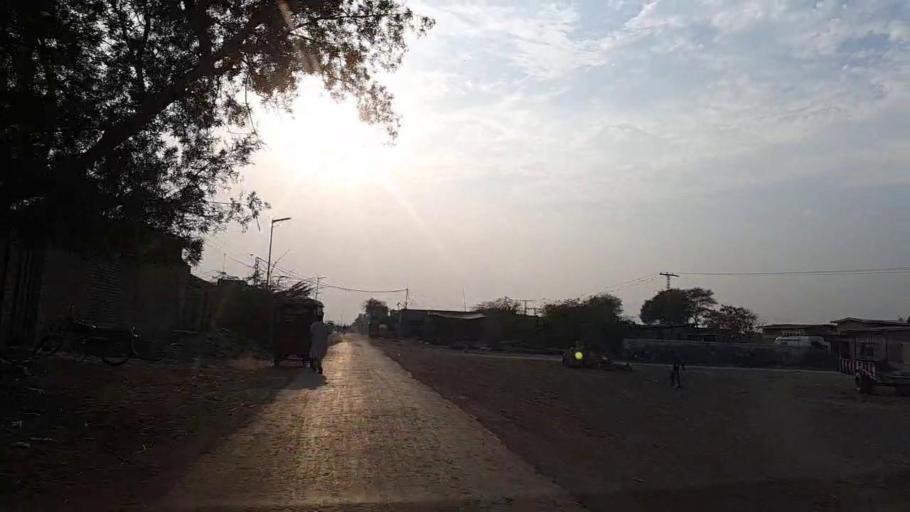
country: PK
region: Sindh
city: Mirwah Gorchani
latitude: 25.3078
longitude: 69.2095
